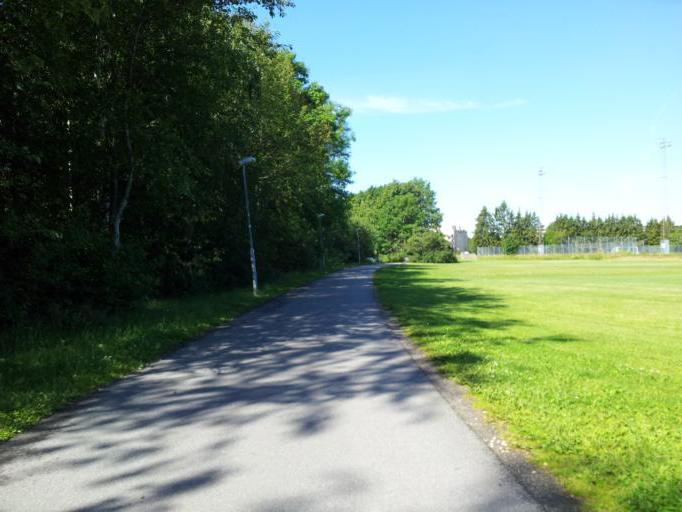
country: SE
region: Uppsala
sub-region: Uppsala Kommun
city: Saevja
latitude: 59.8606
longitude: 17.6950
